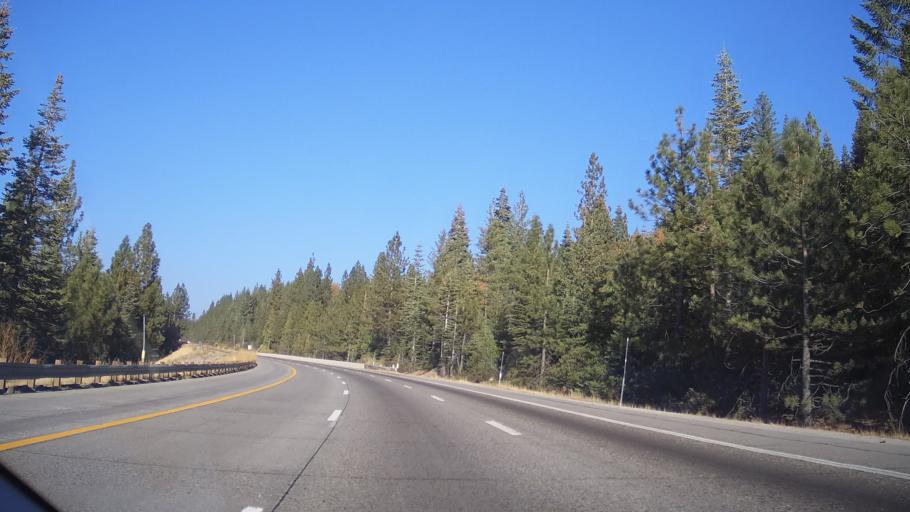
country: US
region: California
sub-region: Placer County
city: Foresthill
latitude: 39.2558
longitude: -120.7320
